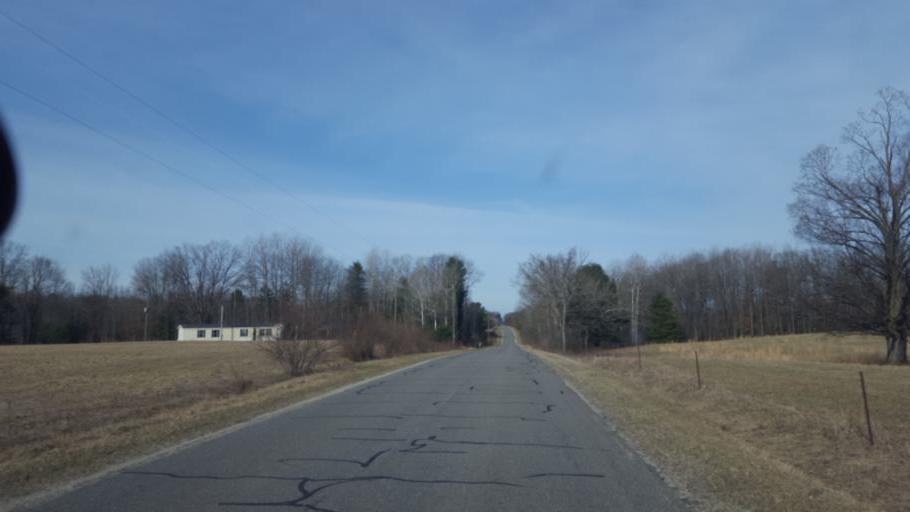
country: US
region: Michigan
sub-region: Montcalm County
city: Howard City
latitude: 43.5258
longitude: -85.5300
